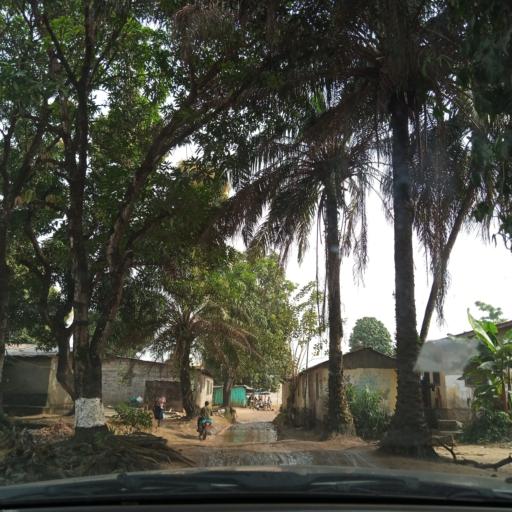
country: LR
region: Montserrado
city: Monrovia
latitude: 6.3371
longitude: -10.7475
